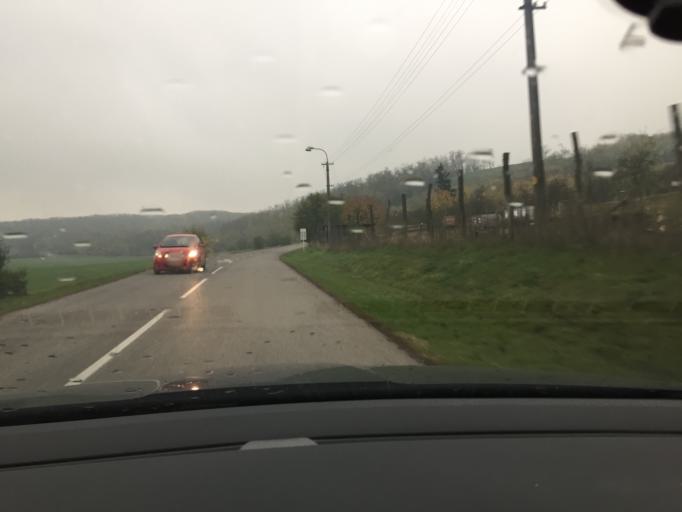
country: SK
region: Banskobystricky
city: Dudince
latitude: 48.0814
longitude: 18.8007
